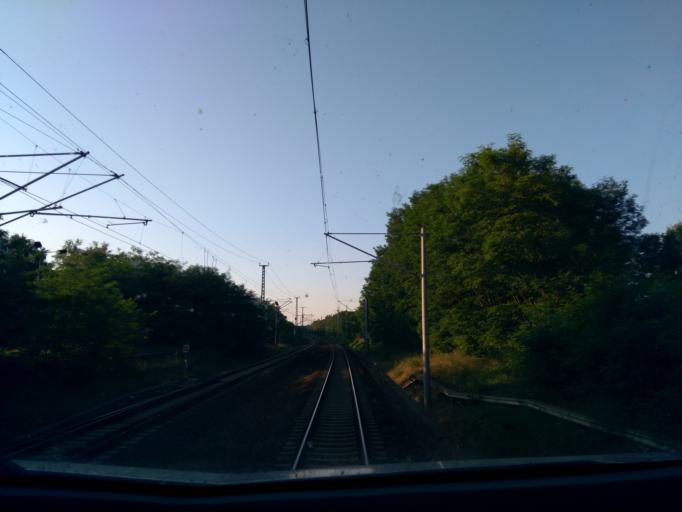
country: DE
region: Brandenburg
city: Halbe
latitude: 52.1063
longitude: 13.7040
